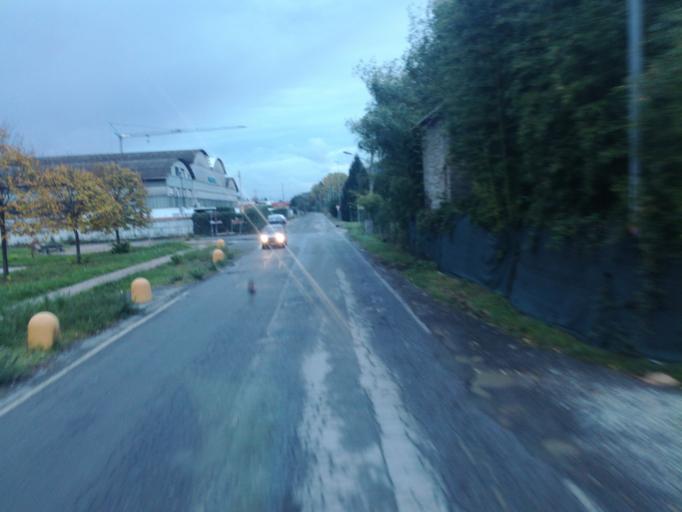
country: IT
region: Liguria
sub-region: Provincia di La Spezia
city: Arcola
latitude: 44.1210
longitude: 9.9176
